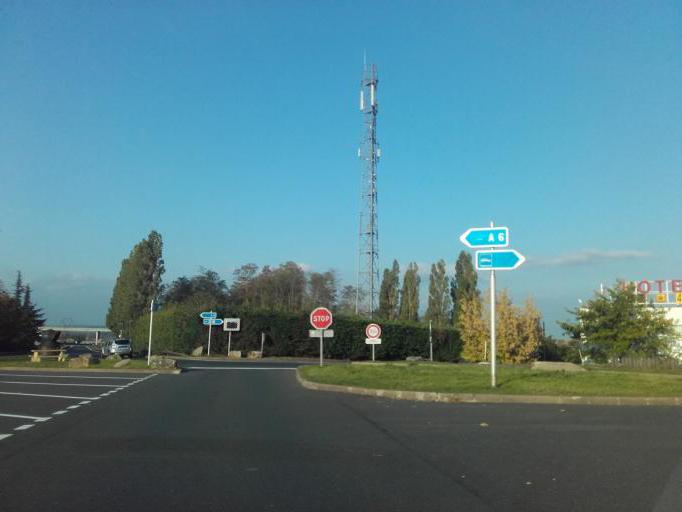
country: FR
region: Bourgogne
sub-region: Departement de Saone-et-Loire
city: Saint-Martin-Belle-Roche
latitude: 46.4207
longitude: 4.8667
